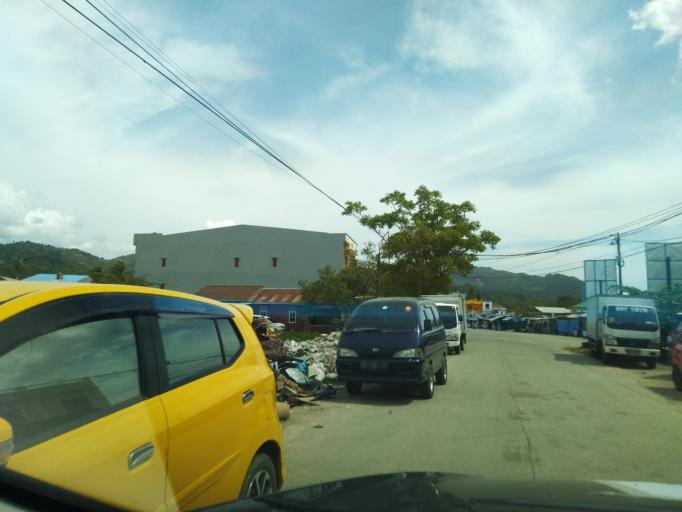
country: ID
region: Sulawesi Barat
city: Mamuju
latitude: -2.6851
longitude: 118.8790
